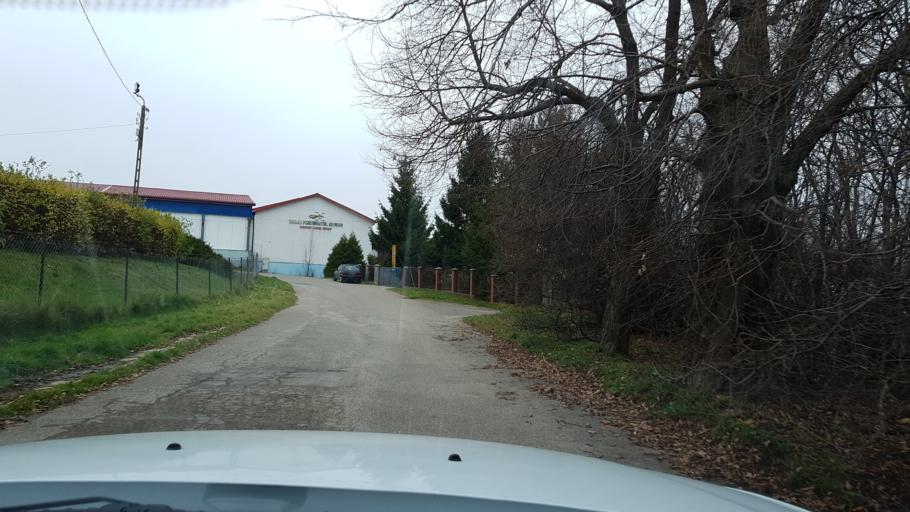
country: PL
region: West Pomeranian Voivodeship
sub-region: Powiat slawienski
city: Darlowo
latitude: 54.4249
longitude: 16.4202
